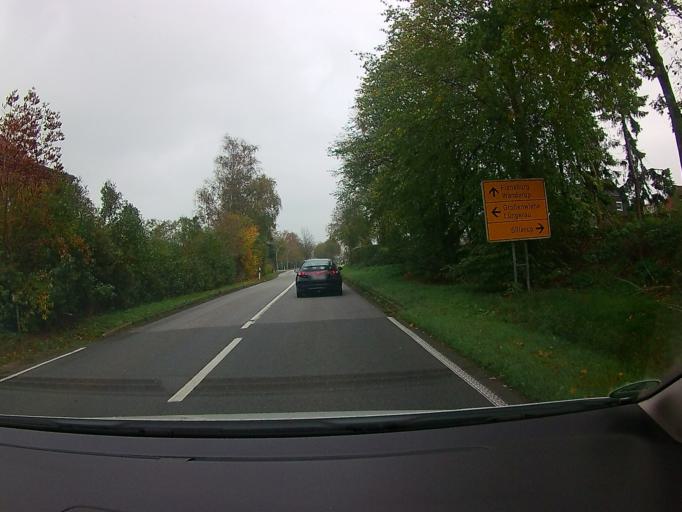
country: DE
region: Schleswig-Holstein
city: Grossenwiehe
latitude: 54.6949
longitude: 9.2418
